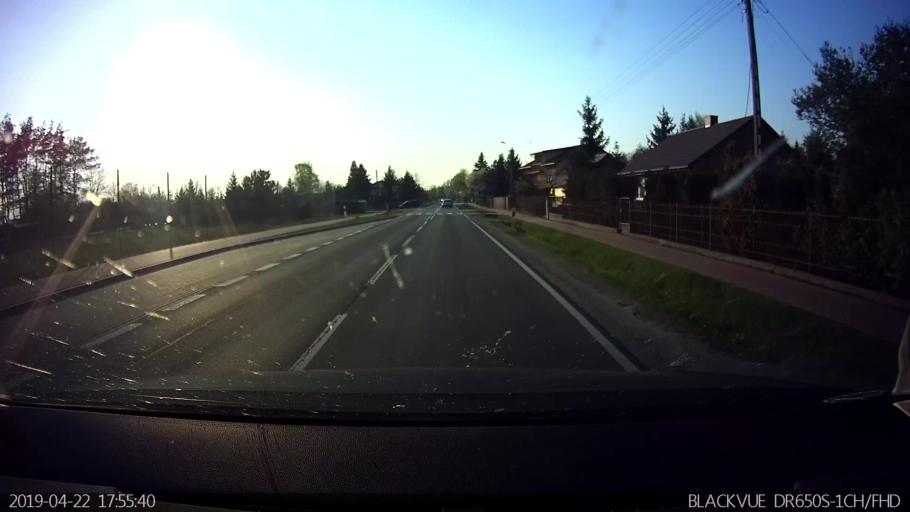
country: PL
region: Masovian Voivodeship
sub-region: Powiat wegrowski
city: Korytnica
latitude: 52.4624
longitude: 21.9163
